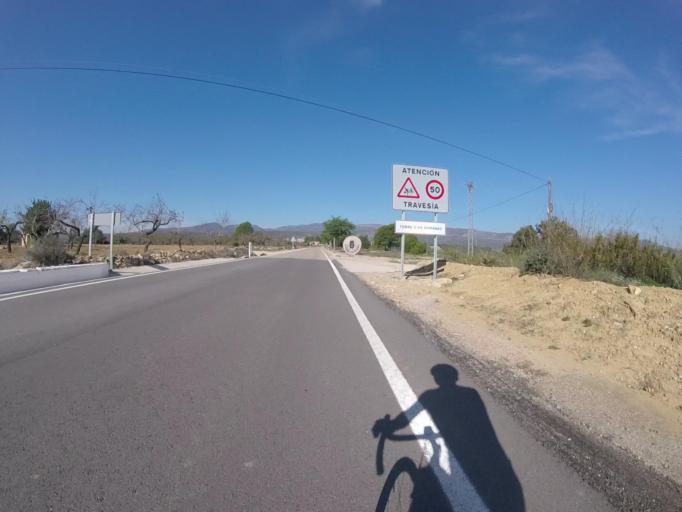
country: ES
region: Valencia
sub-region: Provincia de Castello
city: Cuevas de Vinroma
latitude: 40.2605
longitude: 0.0774
